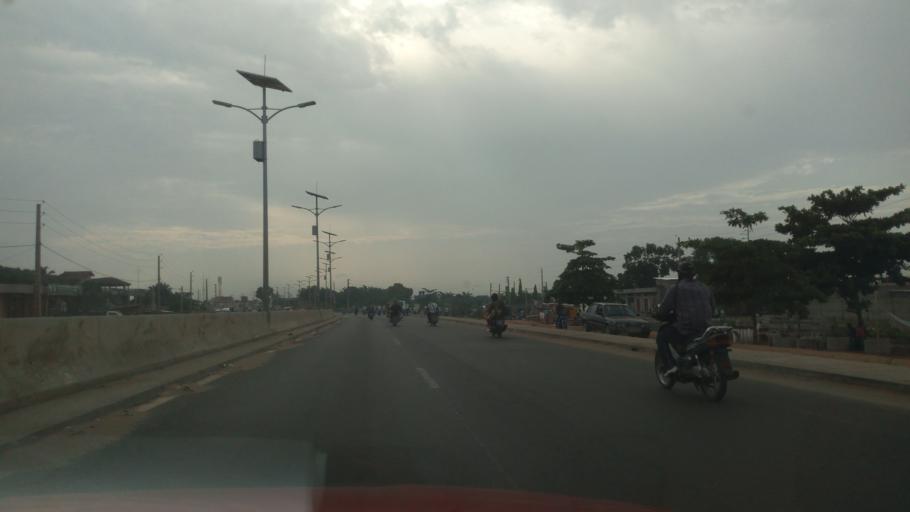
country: BJ
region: Atlantique
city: Hevie
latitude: 6.3864
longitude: 2.2917
